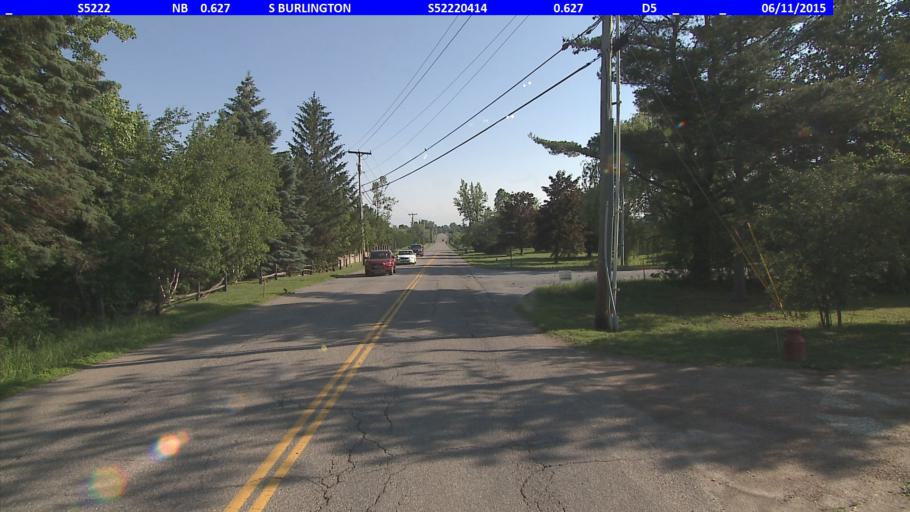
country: US
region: Vermont
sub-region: Chittenden County
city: South Burlington
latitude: 44.4258
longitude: -73.1947
